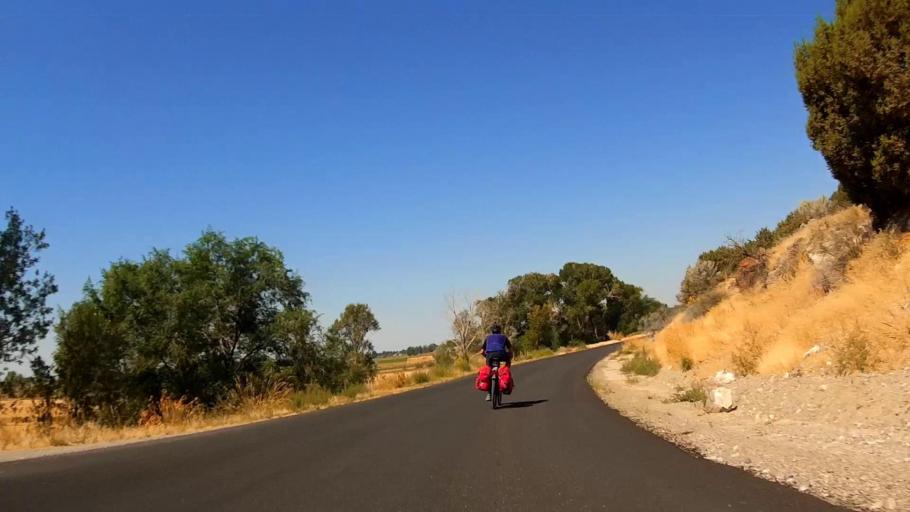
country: US
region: Idaho
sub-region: Madison County
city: Rexburg
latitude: 43.7152
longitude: -111.7535
